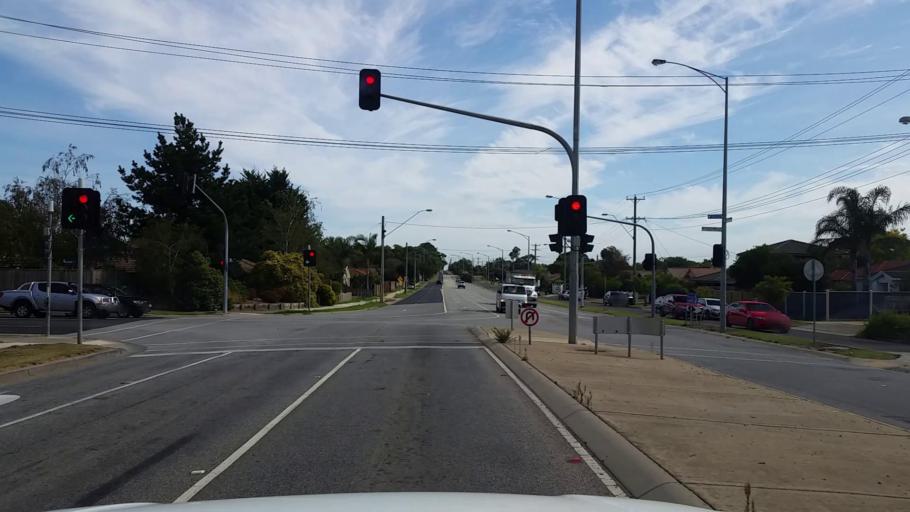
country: AU
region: Victoria
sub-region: Frankston
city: Carrum Downs
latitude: -38.1169
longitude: 145.1918
